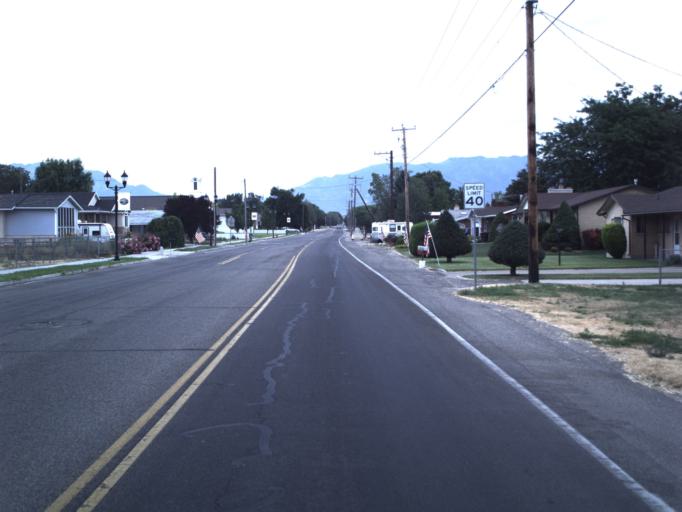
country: US
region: Utah
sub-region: Davis County
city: West Point
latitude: 41.1181
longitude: -112.0833
